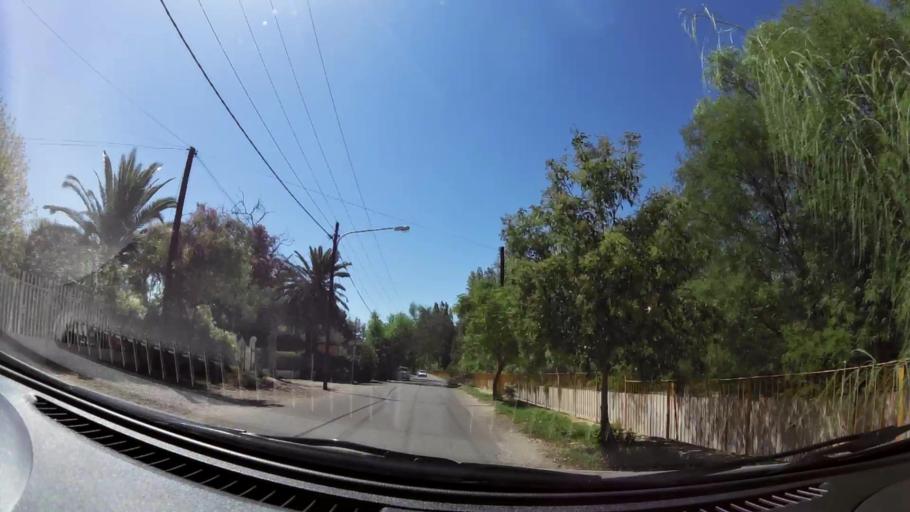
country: AR
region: Mendoza
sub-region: Departamento de Godoy Cruz
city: Godoy Cruz
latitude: -32.9658
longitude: -68.8673
